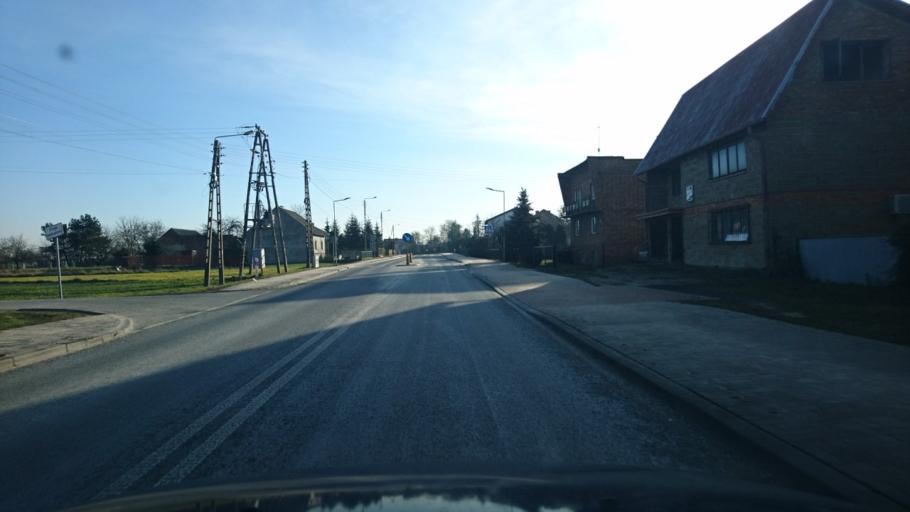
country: PL
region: Silesian Voivodeship
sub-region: Powiat klobucki
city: Starokrzepice
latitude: 51.0072
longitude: 18.6584
